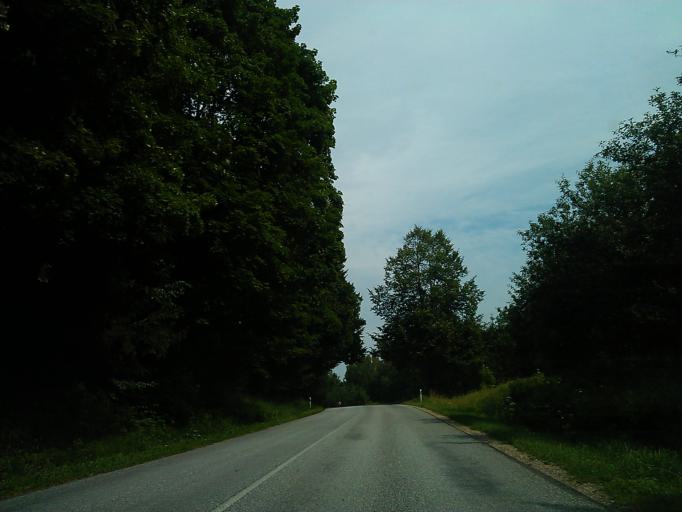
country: LV
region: Beverina
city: Murmuiza
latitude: 57.4062
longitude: 25.4326
